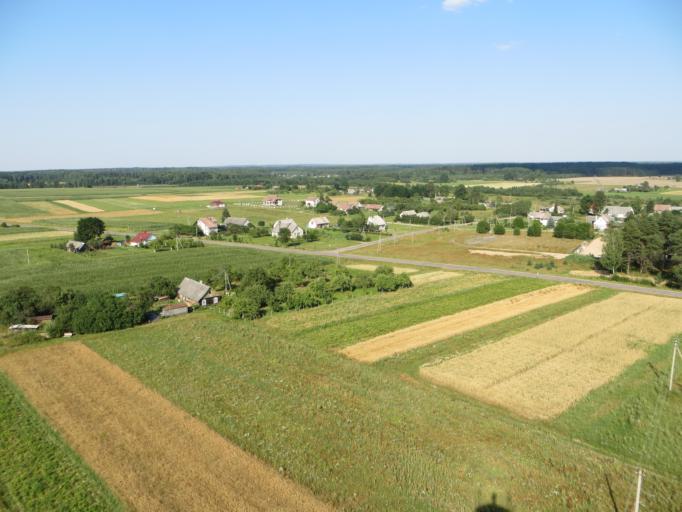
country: LT
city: Salcininkai
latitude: 54.3316
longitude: 25.3129
